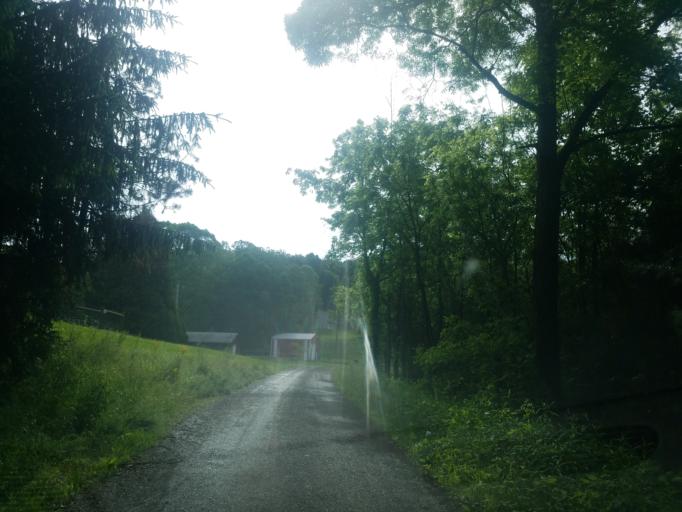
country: US
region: Ohio
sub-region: Holmes County
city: Millersburg
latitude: 40.5171
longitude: -81.8752
